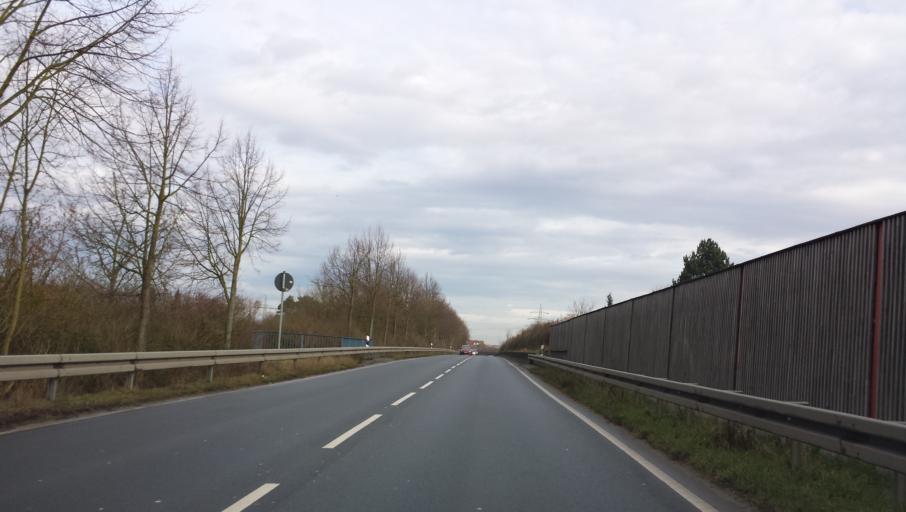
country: DE
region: Hesse
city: Weiterstadt
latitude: 49.9067
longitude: 8.5766
